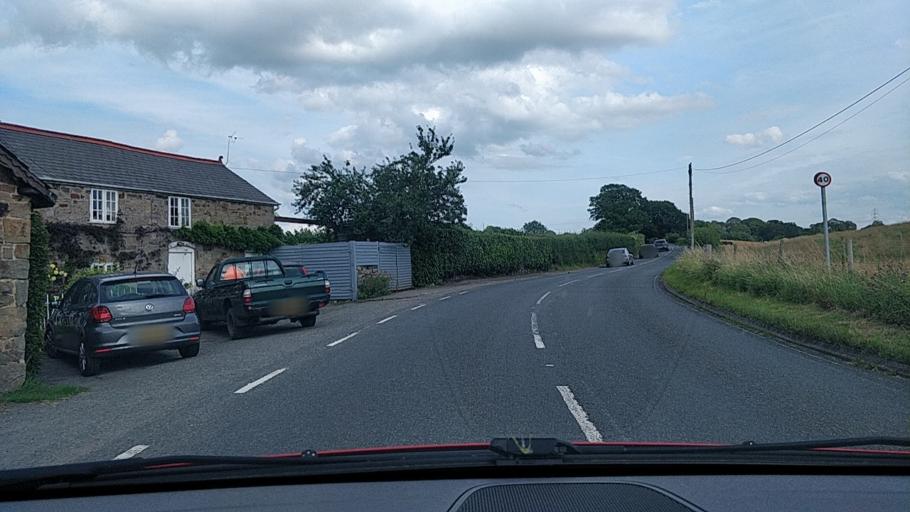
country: GB
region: Wales
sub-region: County of Flintshire
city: Penyffordd
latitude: 53.1420
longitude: -3.0647
